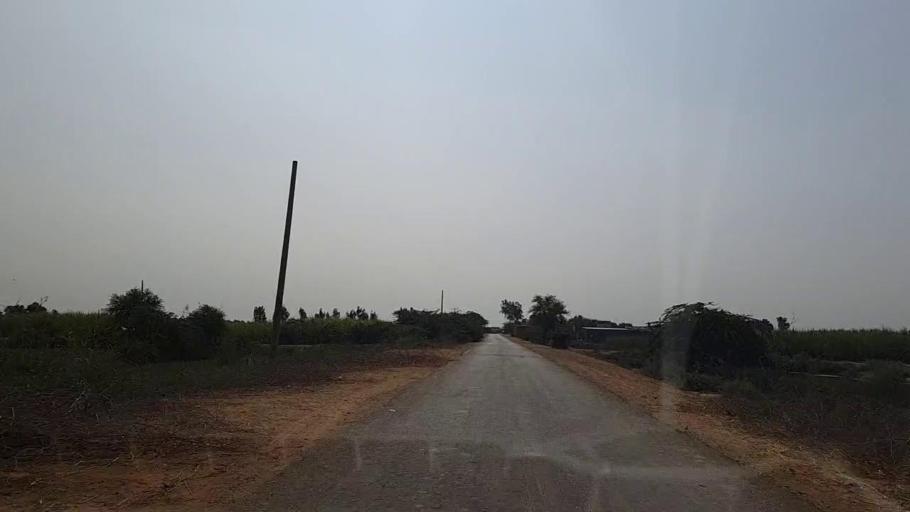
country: PK
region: Sindh
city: Chuhar Jamali
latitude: 24.3128
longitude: 67.9393
